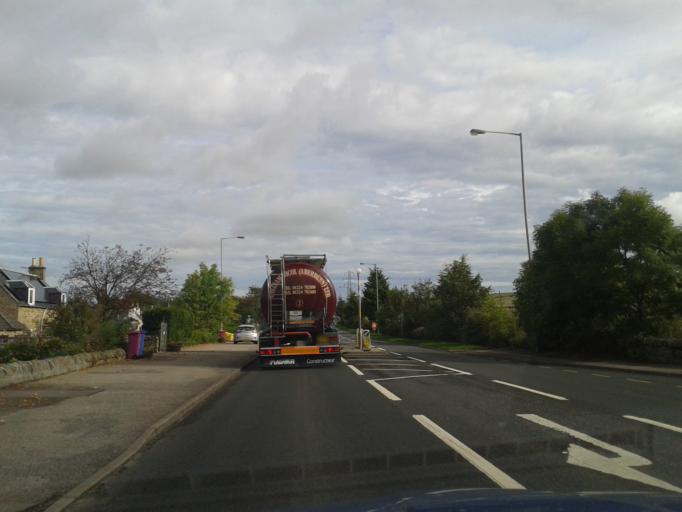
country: GB
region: Scotland
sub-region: Moray
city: Hopeman
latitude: 57.6410
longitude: -3.4525
